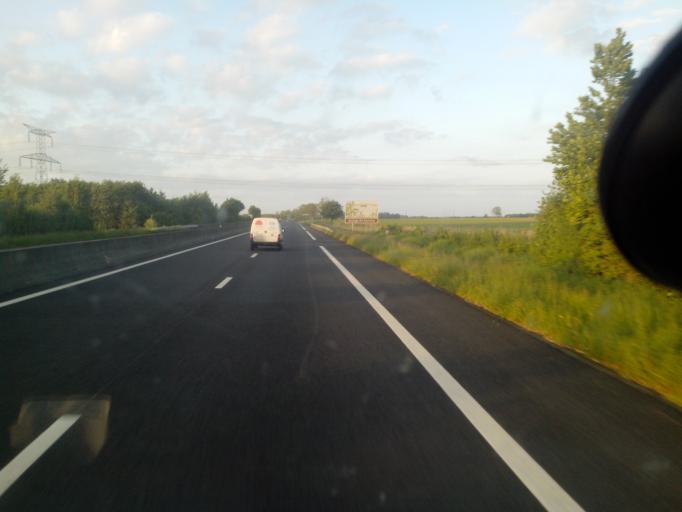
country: FR
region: Picardie
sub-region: Departement de la Somme
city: Oisemont
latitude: 50.0262
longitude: 1.7350
